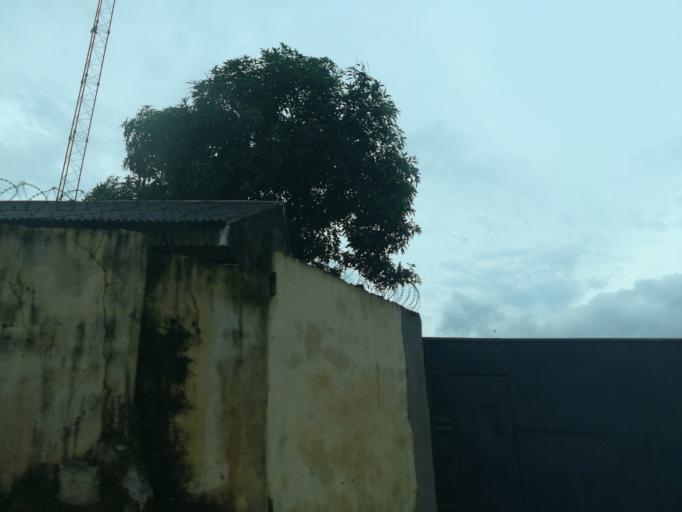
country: NG
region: Rivers
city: Port Harcourt
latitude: 4.8545
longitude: 7.0361
